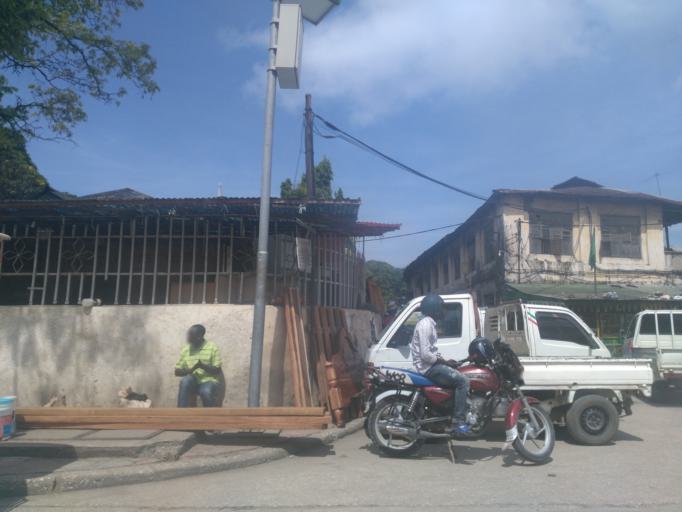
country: TZ
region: Zanzibar Urban/West
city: Zanzibar
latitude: -6.1632
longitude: 39.1935
